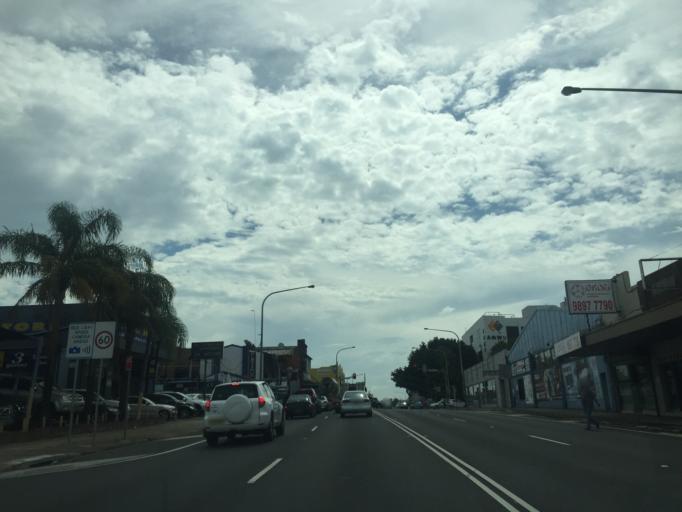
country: AU
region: New South Wales
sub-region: Parramatta
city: Granville
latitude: -33.8311
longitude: 151.0133
